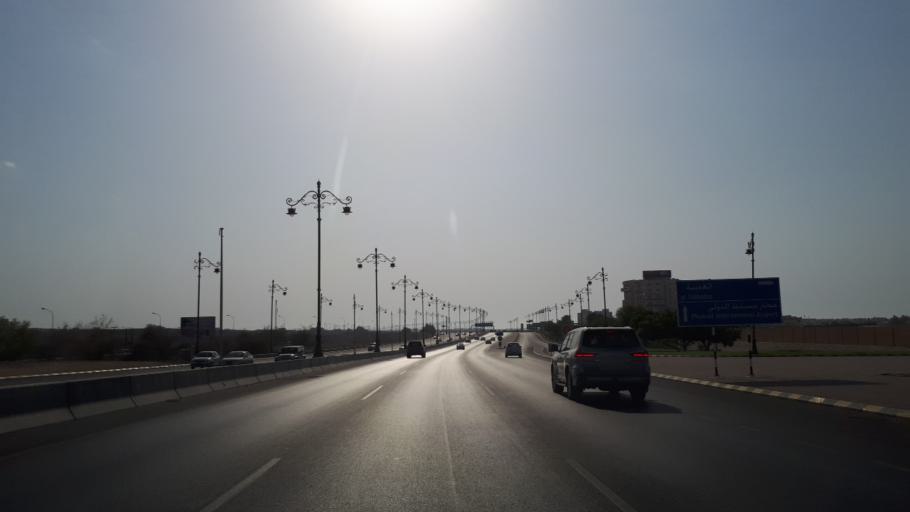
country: OM
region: Muhafazat Masqat
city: Bawshar
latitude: 23.5897
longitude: 58.3553
